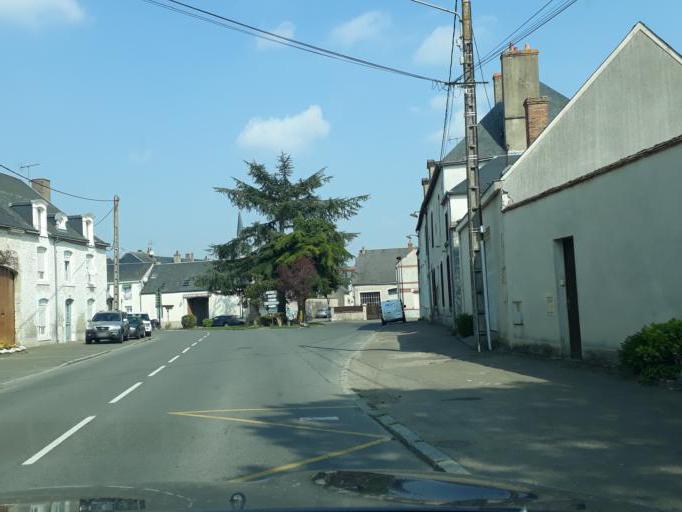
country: FR
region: Centre
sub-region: Departement du Loiret
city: Artenay
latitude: 48.0807
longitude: 1.8787
